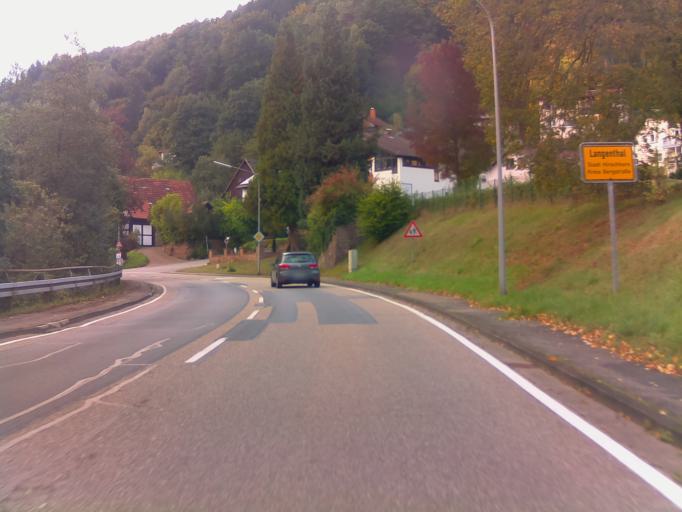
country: DE
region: Baden-Wuerttemberg
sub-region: Karlsruhe Region
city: Heddesbach
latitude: 49.4720
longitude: 8.8501
